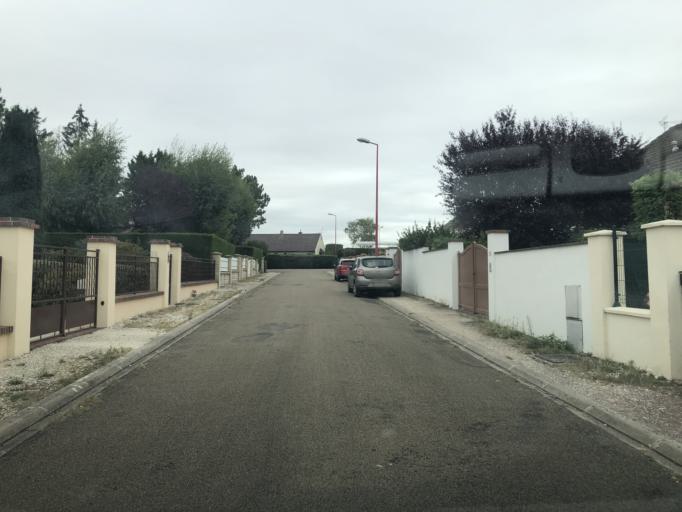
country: FR
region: Bourgogne
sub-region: Departement de l'Yonne
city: Aillant-sur-Tholon
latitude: 47.8772
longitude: 3.3600
